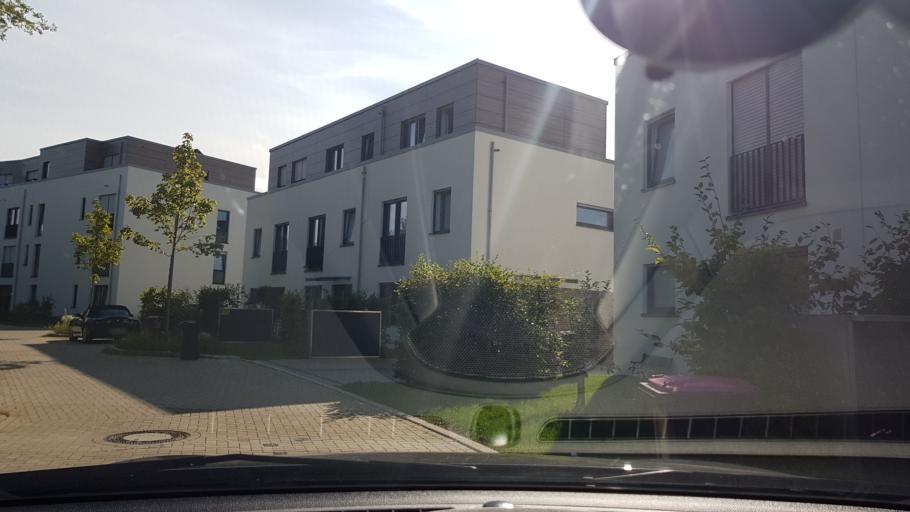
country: DE
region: North Rhine-Westphalia
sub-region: Regierungsbezirk Dusseldorf
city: Neuss
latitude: 51.1530
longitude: 6.6953
